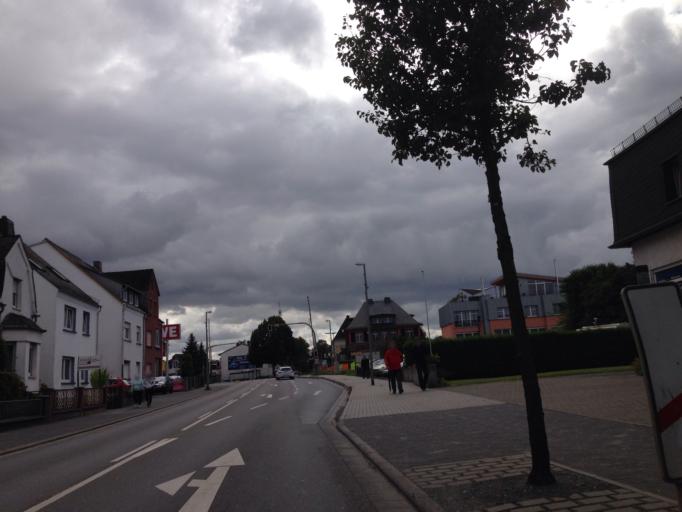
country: DE
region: Hesse
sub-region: Regierungsbezirk Giessen
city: Elz
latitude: 50.4074
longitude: 8.0362
